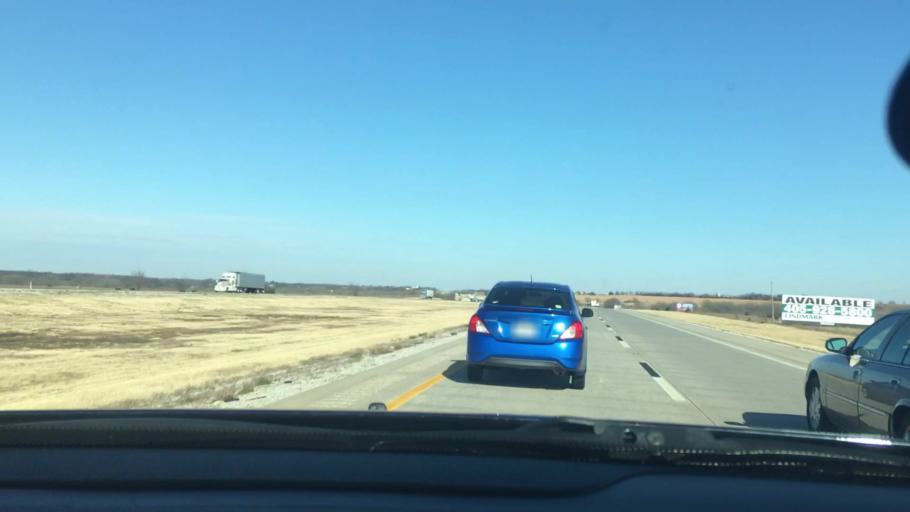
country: US
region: Oklahoma
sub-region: Carter County
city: Ardmore
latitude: 34.0983
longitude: -97.1511
